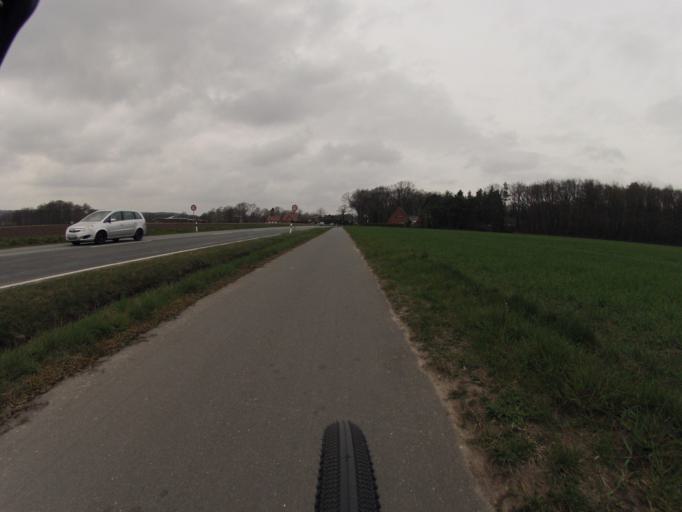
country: DE
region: North Rhine-Westphalia
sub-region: Regierungsbezirk Munster
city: Mettingen
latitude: 52.3346
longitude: 7.7454
